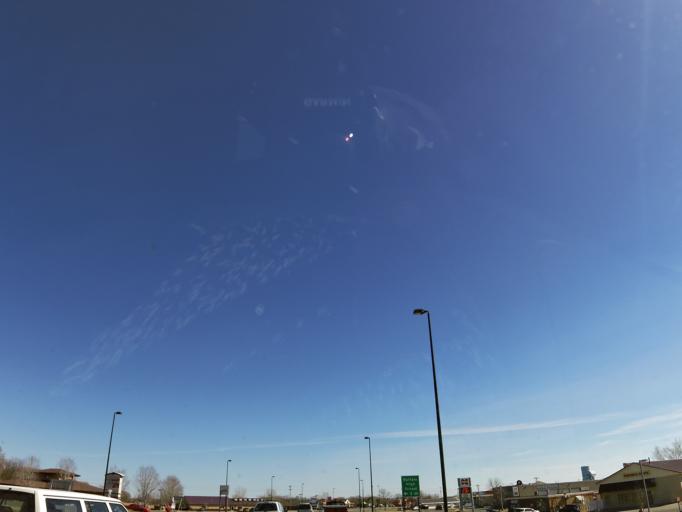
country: US
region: Minnesota
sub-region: Wright County
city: Buffalo
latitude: 45.1792
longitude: -93.8710
